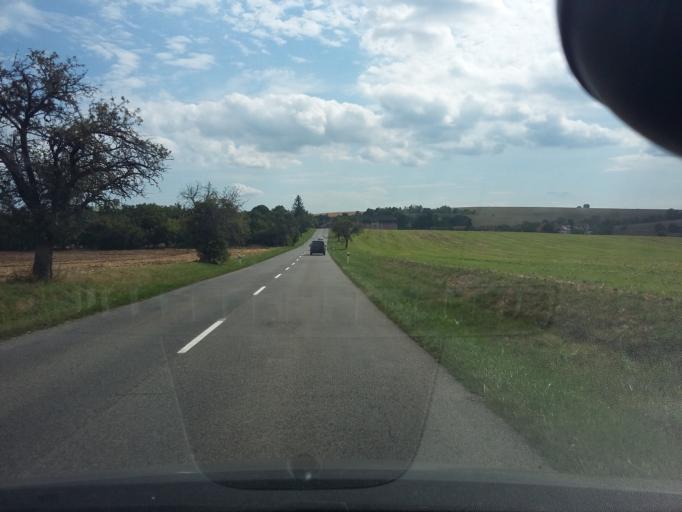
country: SK
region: Trnavsky
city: Gbely
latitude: 48.7298
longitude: 17.1635
